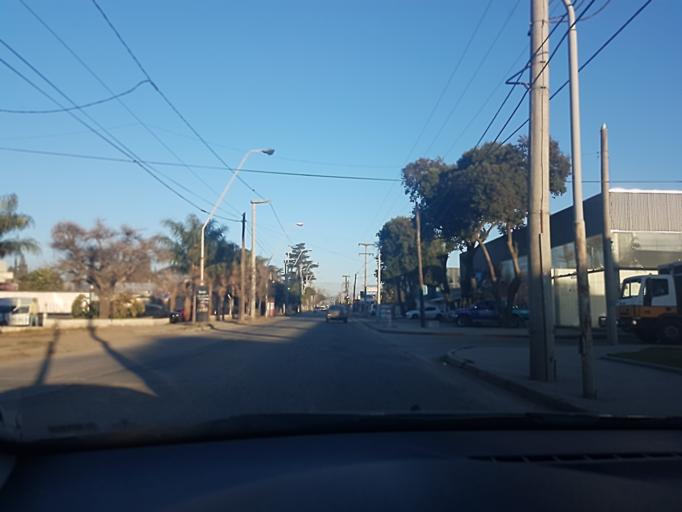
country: AR
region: Cordoba
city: Villa Allende
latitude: -31.3433
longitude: -64.2360
